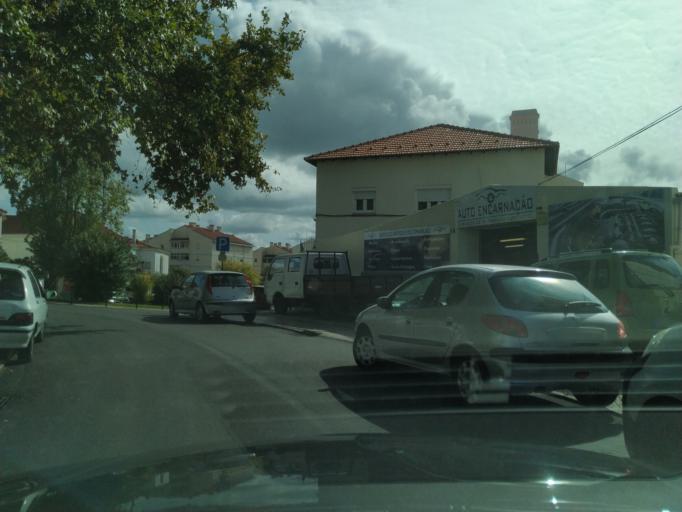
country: PT
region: Lisbon
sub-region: Loures
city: Moscavide
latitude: 38.7715
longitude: -9.1137
